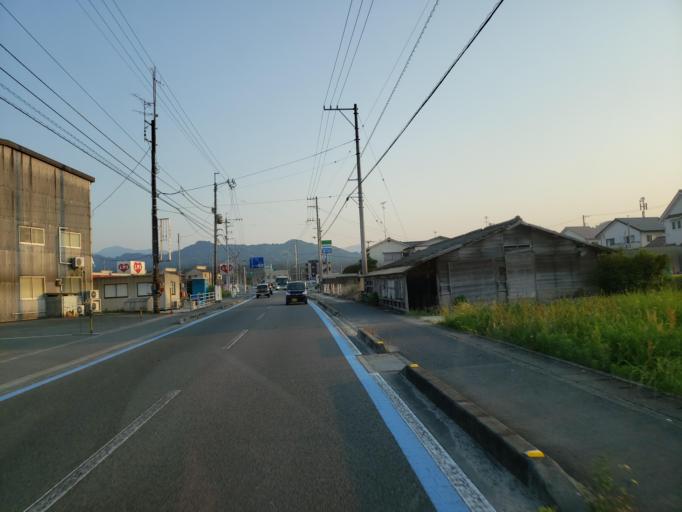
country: JP
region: Ehime
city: Hojo
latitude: 34.0395
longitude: 132.9743
